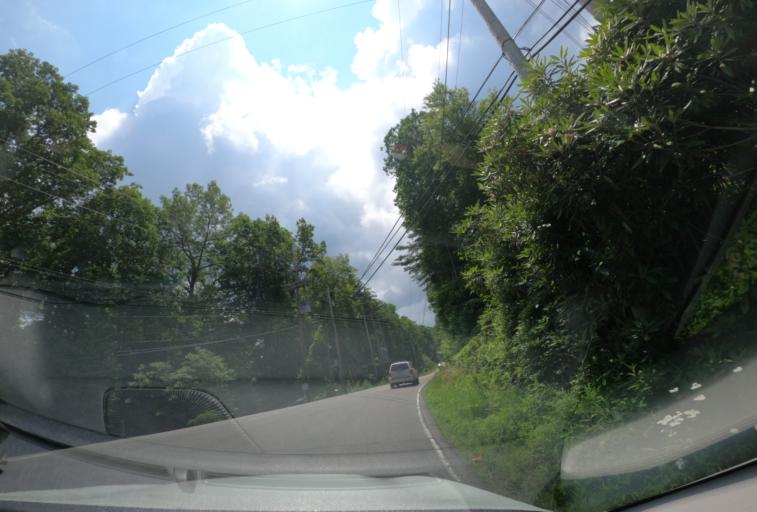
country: US
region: North Carolina
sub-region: Macon County
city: Franklin
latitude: 35.0619
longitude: -83.2098
